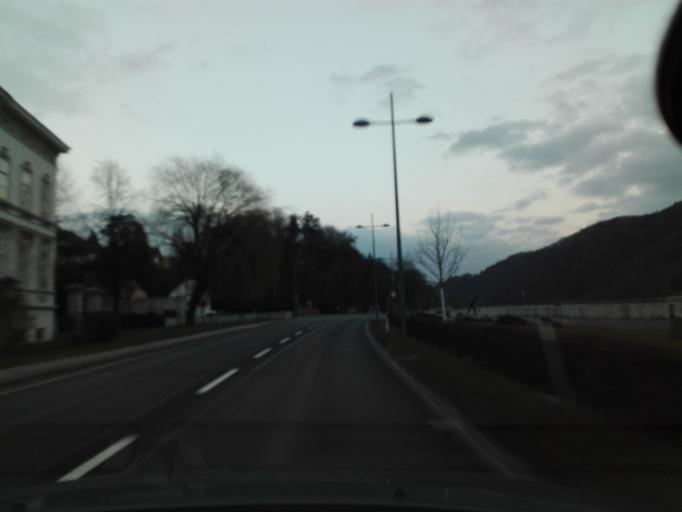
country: AT
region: Upper Austria
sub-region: Politischer Bezirk Perg
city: Bad Kreuzen
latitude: 48.2280
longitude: 14.8584
